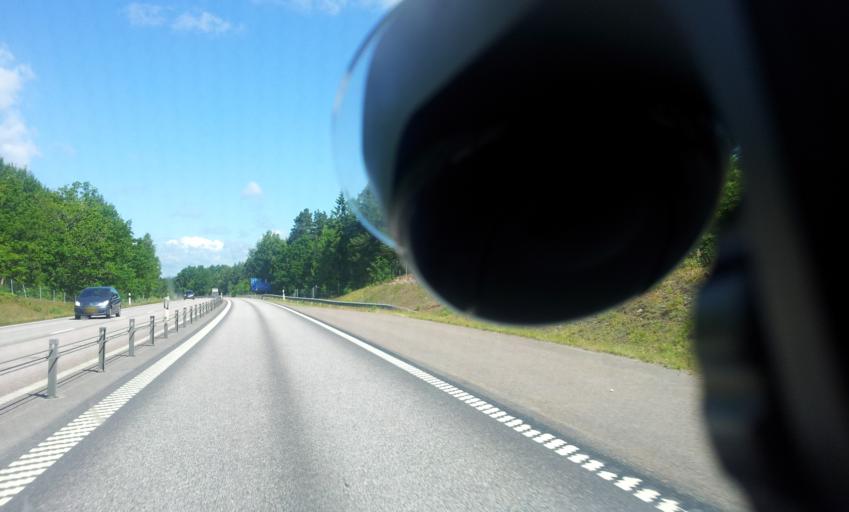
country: SE
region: Kalmar
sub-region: Oskarshamns Kommun
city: Paskallavik
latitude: 57.1450
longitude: 16.4691
